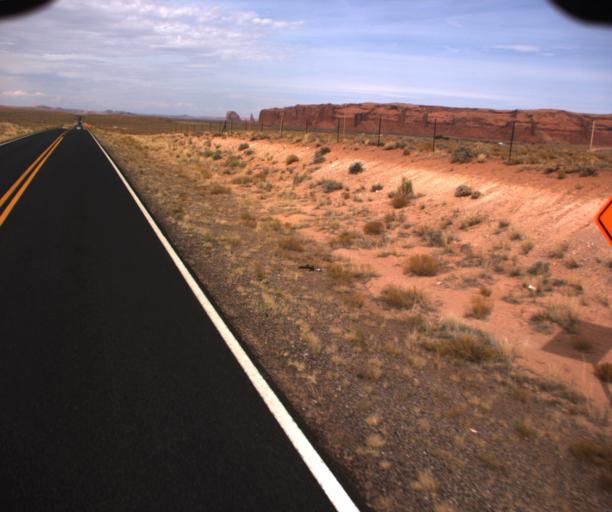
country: US
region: Arizona
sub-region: Apache County
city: Many Farms
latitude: 36.5833
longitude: -109.5567
